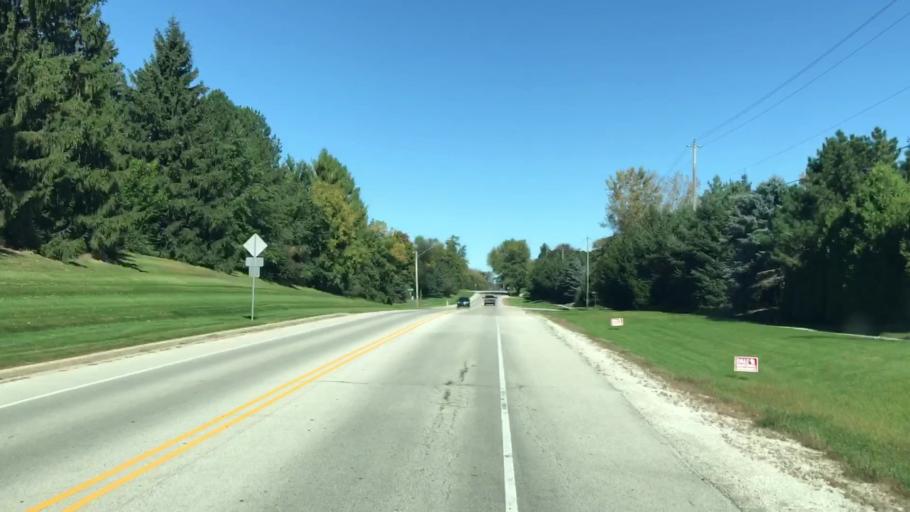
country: US
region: Wisconsin
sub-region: Waukesha County
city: Brookfield
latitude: 43.0630
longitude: -88.1663
